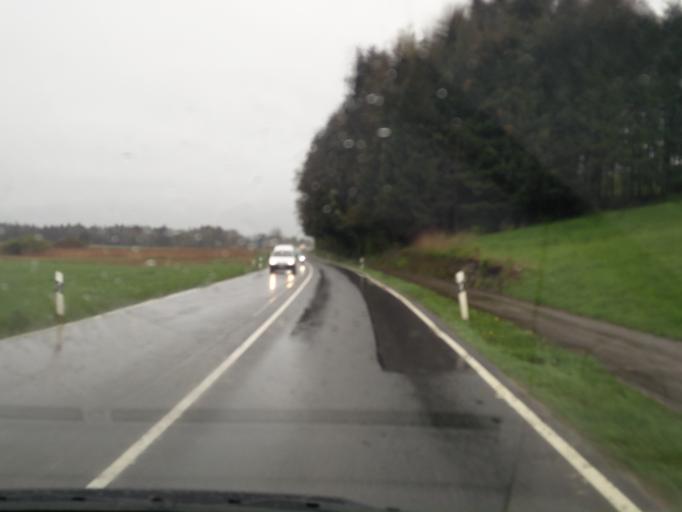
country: DE
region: Bavaria
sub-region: Upper Bavaria
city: Prien am Chiemsee
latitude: 47.8331
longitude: 12.3556
